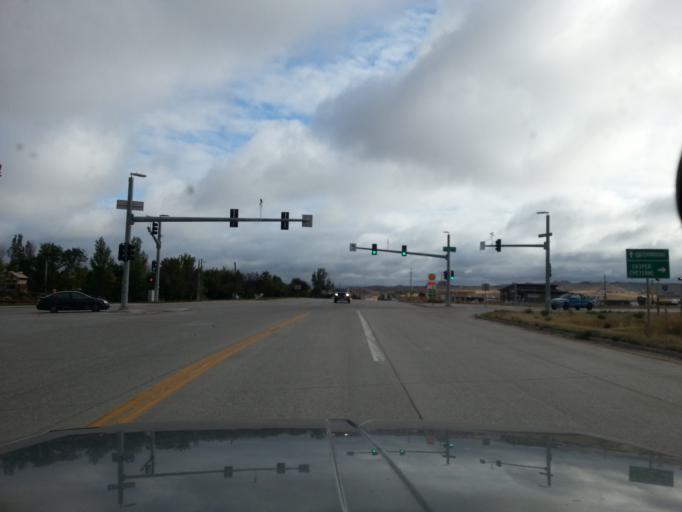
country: US
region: Wyoming
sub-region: Converse County
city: Douglas
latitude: 42.7625
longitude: -105.4067
